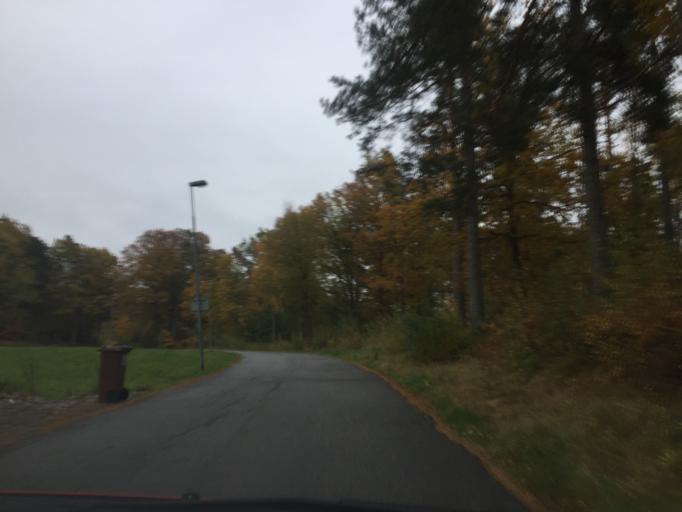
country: SE
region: Vaestra Goetaland
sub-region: Trollhattan
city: Sjuntorp
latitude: 58.2009
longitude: 12.2181
